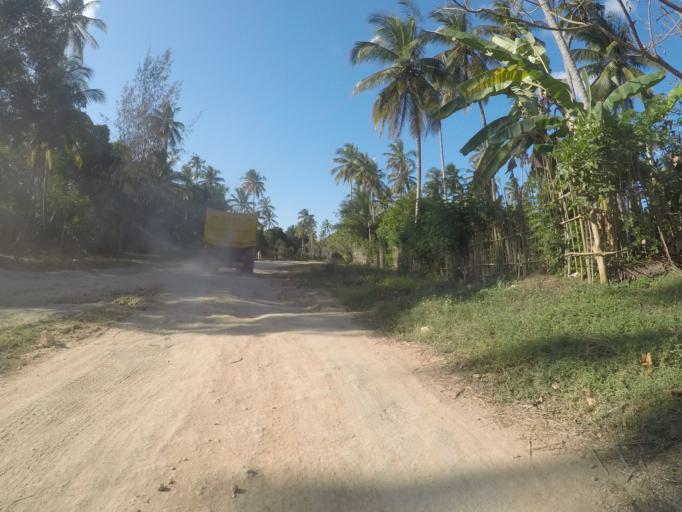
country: TZ
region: Zanzibar Central/South
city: Koani
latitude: -6.1717
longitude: 39.2853
